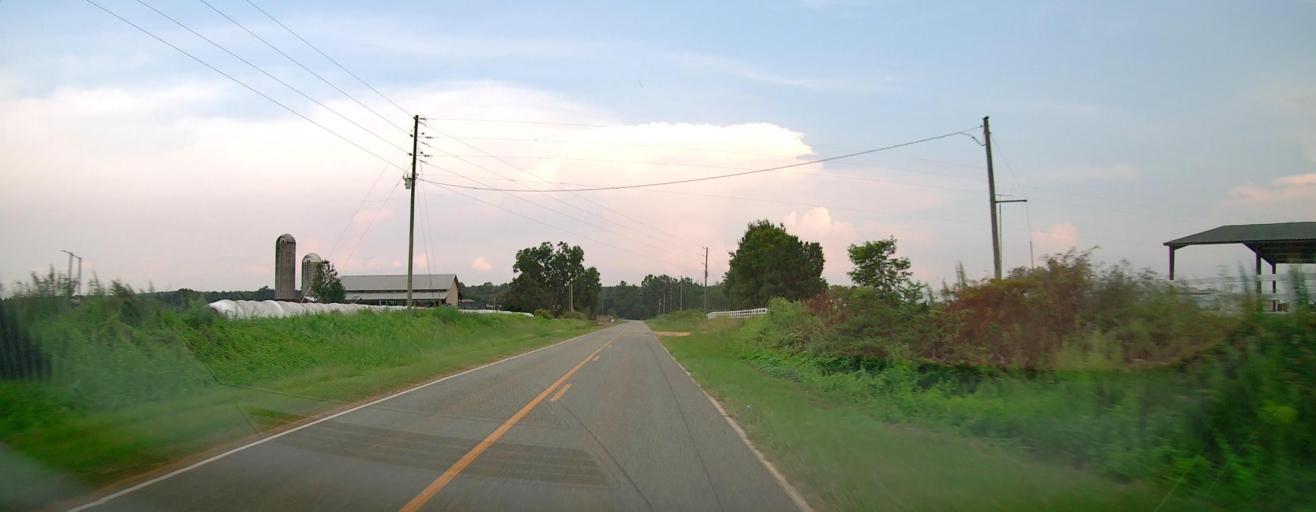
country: US
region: Georgia
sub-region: Laurens County
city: East Dublin
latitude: 32.6429
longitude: -82.8154
